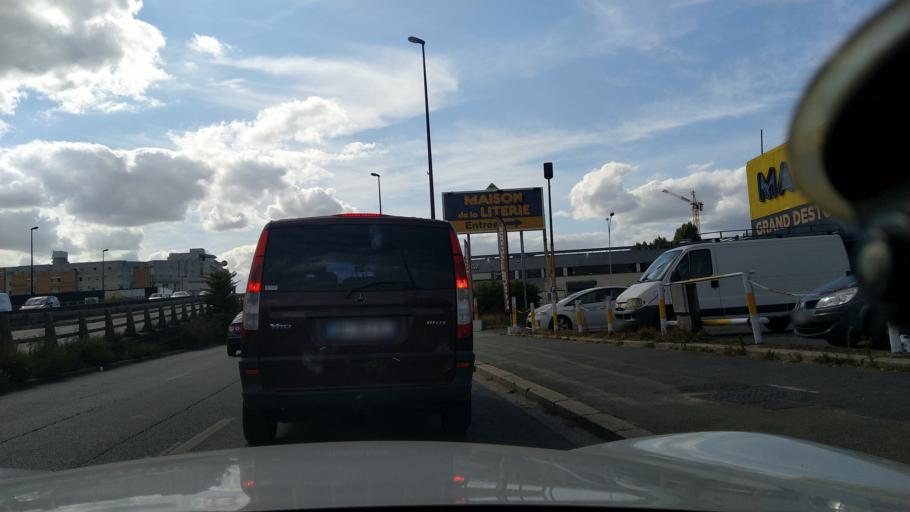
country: FR
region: Ile-de-France
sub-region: Departement de Seine-Saint-Denis
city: Bondy
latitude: 48.9063
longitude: 2.4833
